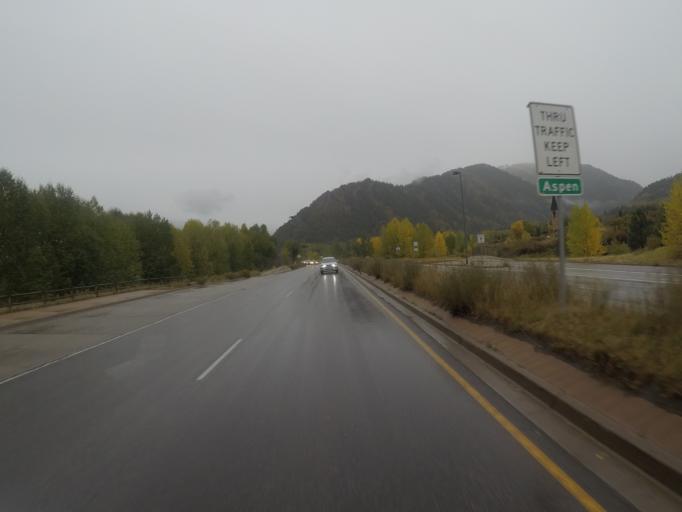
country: US
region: Colorado
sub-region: Pitkin County
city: Aspen
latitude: 39.1968
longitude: -106.8419
